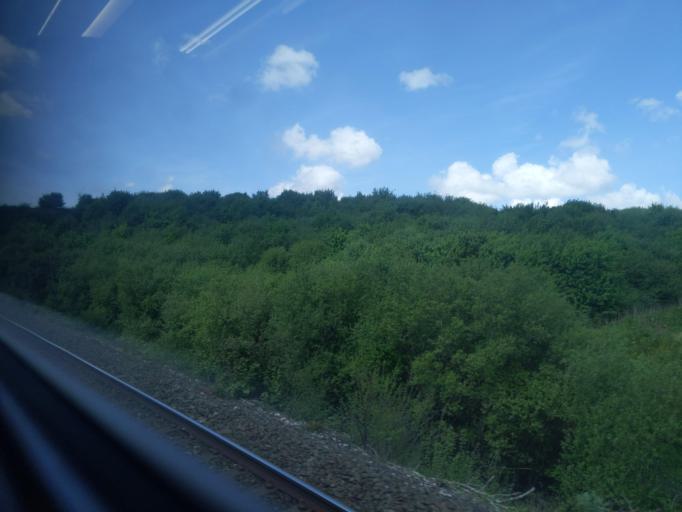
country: GB
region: England
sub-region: Cornwall
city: Liskeard
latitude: 50.4559
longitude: -4.5259
